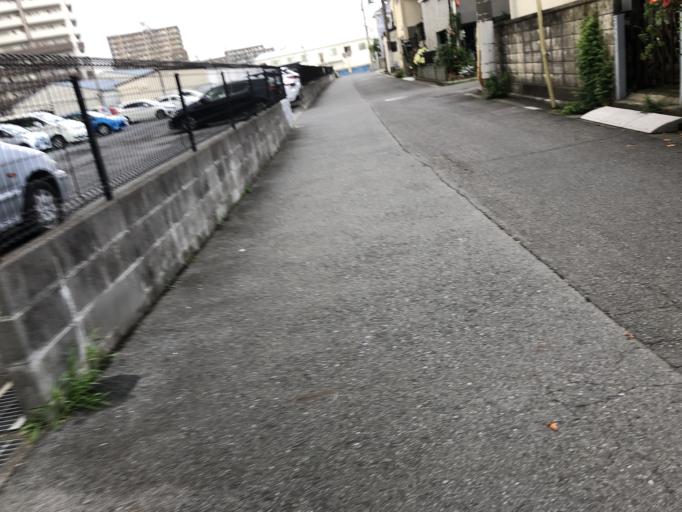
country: JP
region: Saitama
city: Asaka
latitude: 35.8017
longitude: 139.5780
